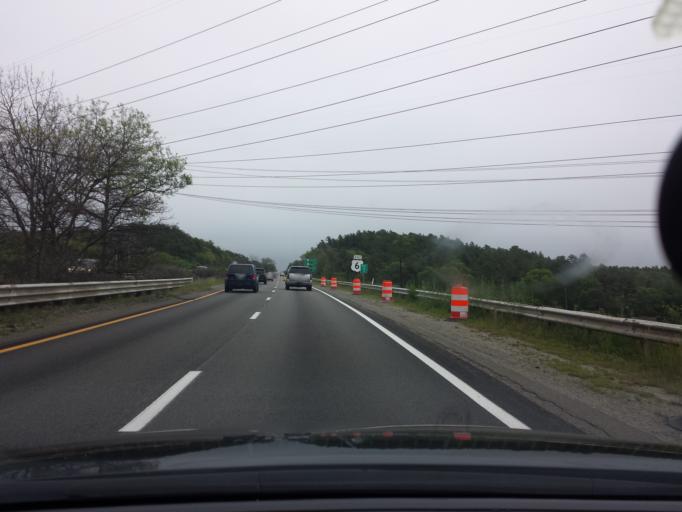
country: US
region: Massachusetts
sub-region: Barnstable County
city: Sagamore
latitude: 41.7649
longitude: -70.5407
